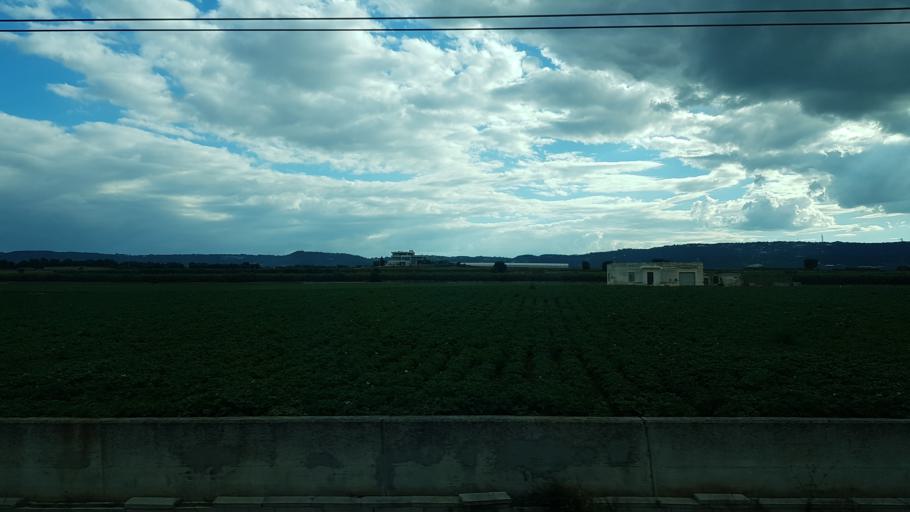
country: IT
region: Apulia
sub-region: Provincia di Brindisi
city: Fasano
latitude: 40.8469
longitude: 17.3929
